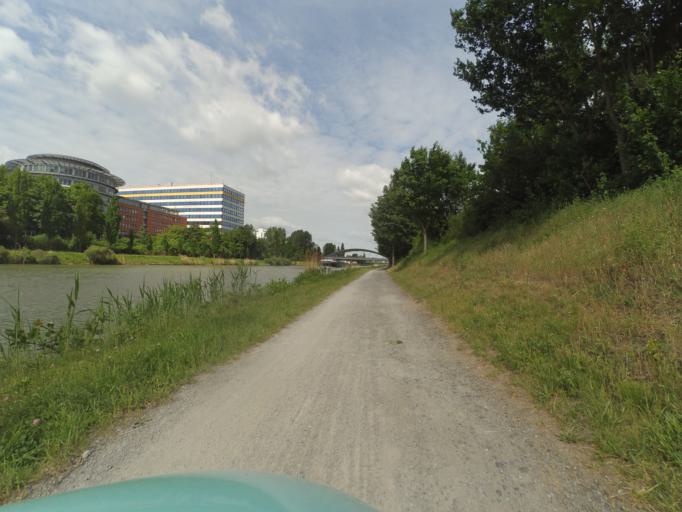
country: DE
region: Lower Saxony
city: Hannover
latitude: 52.4069
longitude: 9.7432
